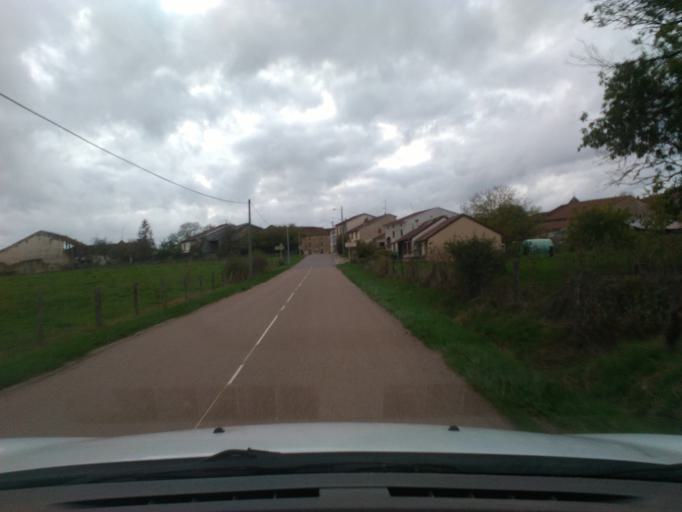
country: FR
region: Lorraine
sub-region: Departement des Vosges
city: Mirecourt
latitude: 48.3512
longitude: 6.0668
